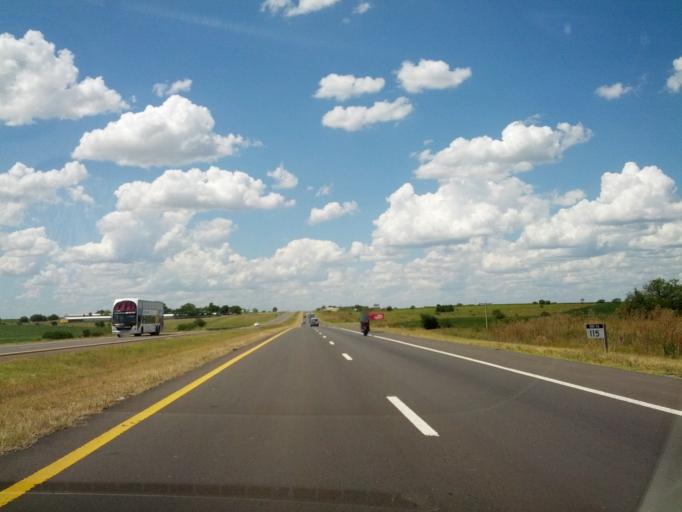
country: AR
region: Entre Rios
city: Colonia Elia
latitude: -32.5593
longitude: -58.3663
